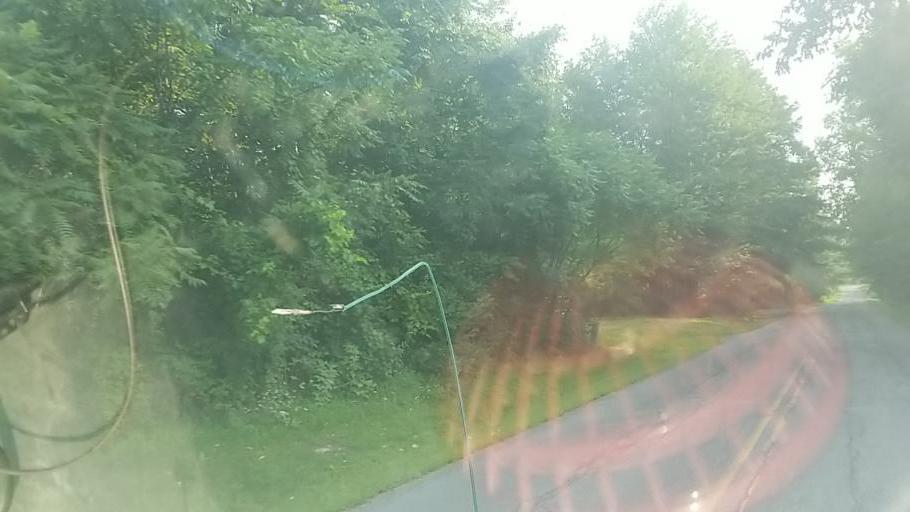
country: US
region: New York
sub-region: Fulton County
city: Broadalbin
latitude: 43.0730
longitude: -74.2311
